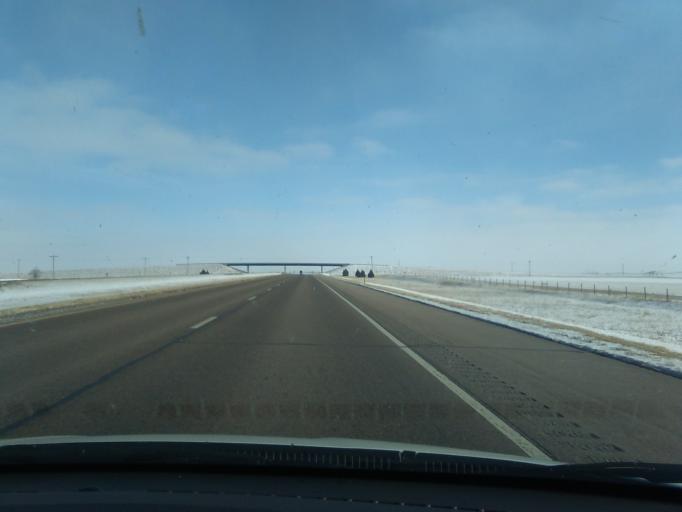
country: US
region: Nebraska
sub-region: Kimball County
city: Kimball
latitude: 41.1917
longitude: -103.8030
